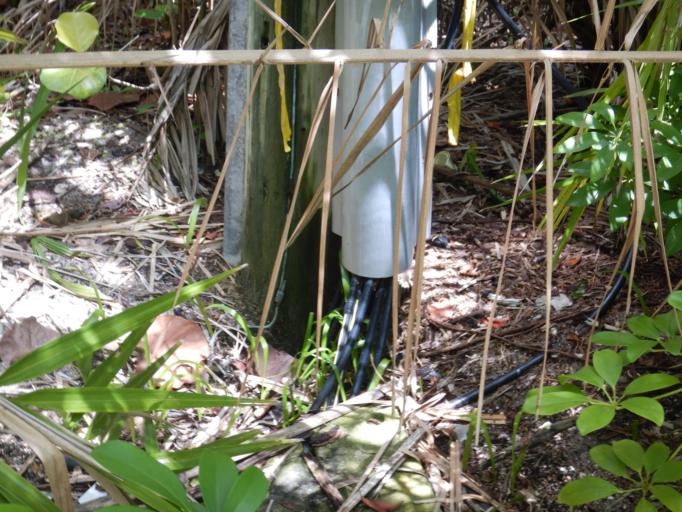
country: US
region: Florida
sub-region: Sarasota County
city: Gulf Gate Estates
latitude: 27.2301
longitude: -82.5220
